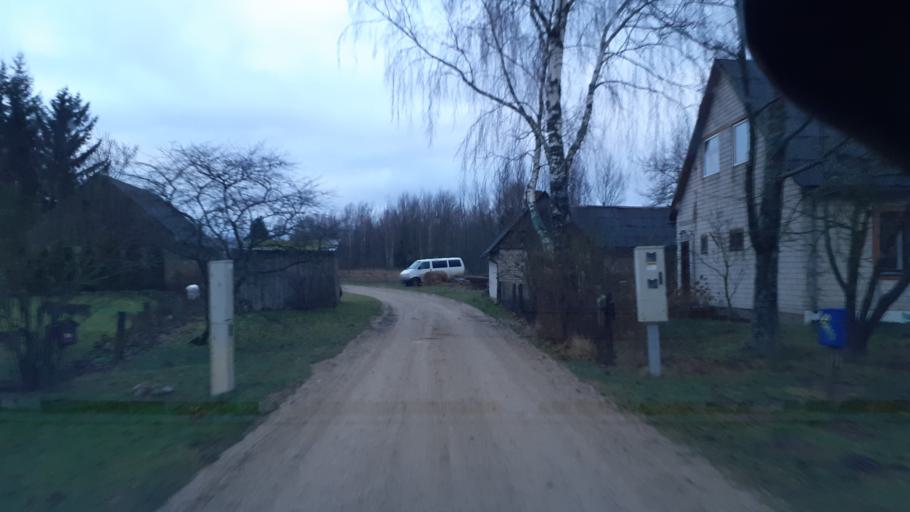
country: LV
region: Alsunga
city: Alsunga
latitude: 56.9043
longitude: 21.6992
